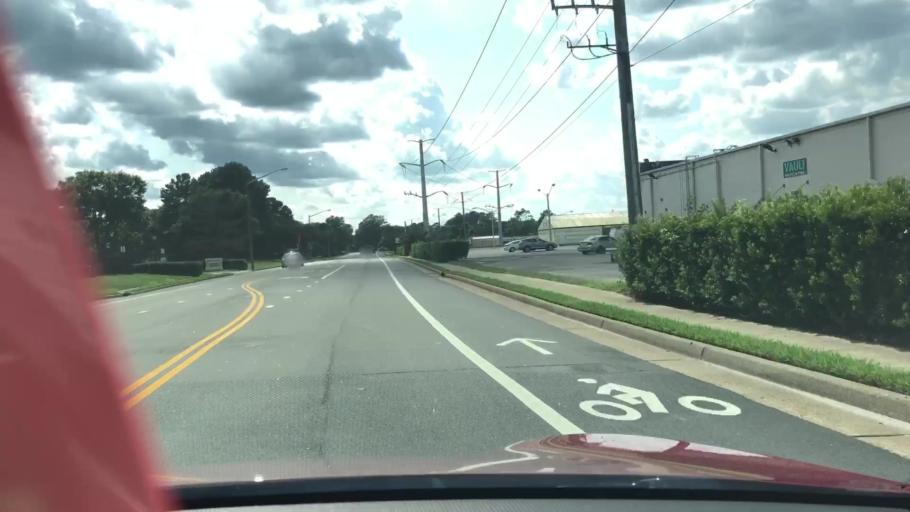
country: US
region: Virginia
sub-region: City of Virginia Beach
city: Virginia Beach
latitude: 36.8480
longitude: -76.0239
